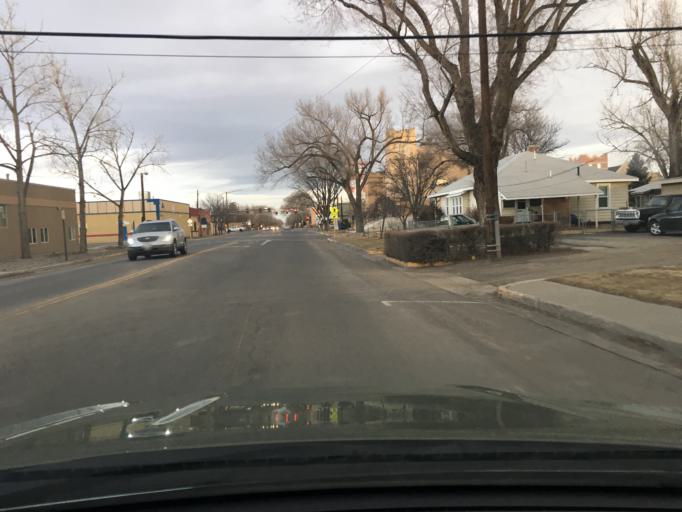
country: US
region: Colorado
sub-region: Montrose County
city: Montrose
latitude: 38.4797
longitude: -107.8732
